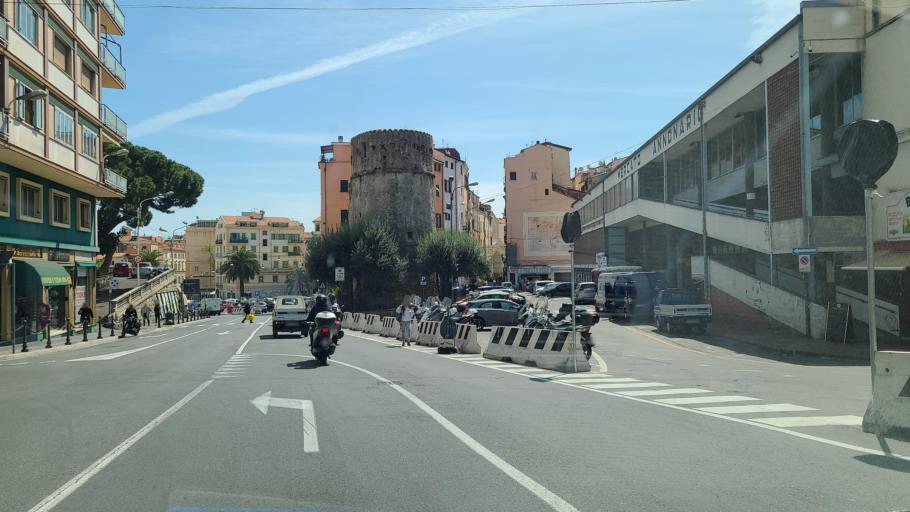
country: IT
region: Liguria
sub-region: Provincia di Imperia
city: San Remo
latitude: 43.8185
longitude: 7.7730
